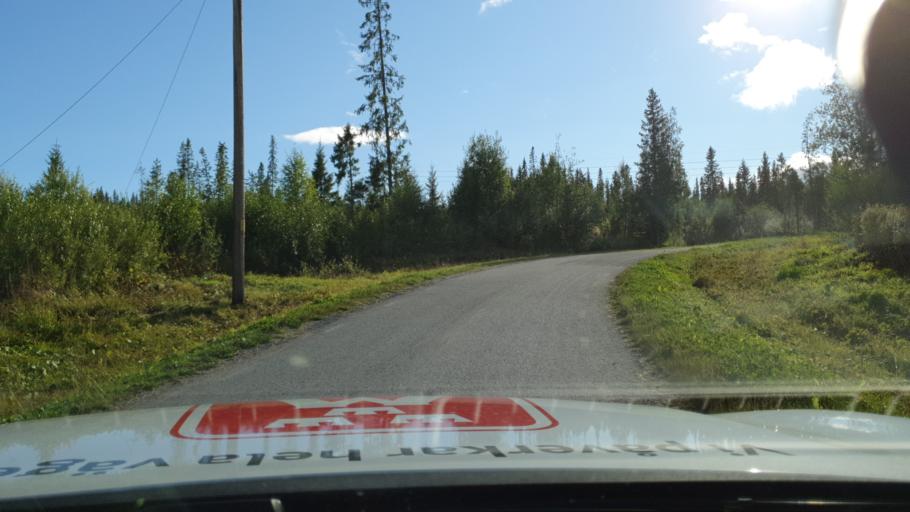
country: SE
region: Jaemtland
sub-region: Stroemsunds Kommun
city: Stroemsund
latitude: 64.4230
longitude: 15.5559
